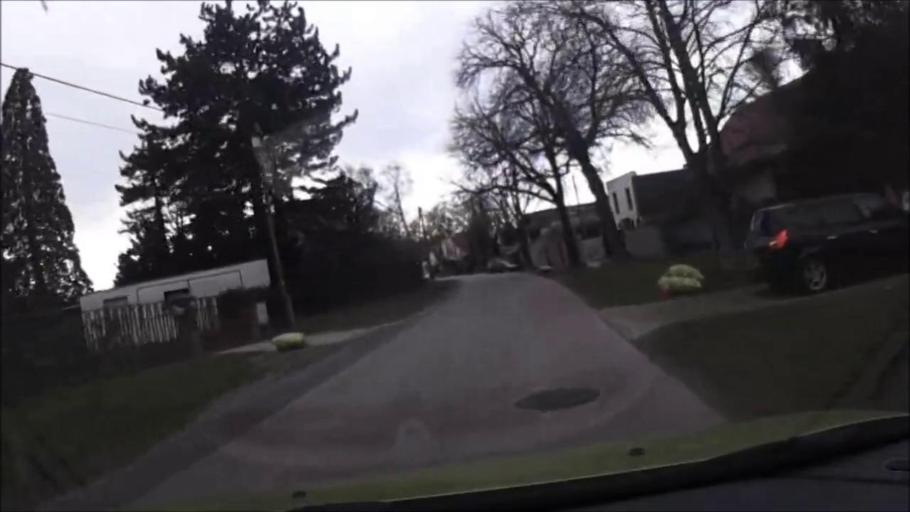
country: AT
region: Lower Austria
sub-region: Politischer Bezirk Baden
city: Ebreichsdorf
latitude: 47.9601
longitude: 16.4344
